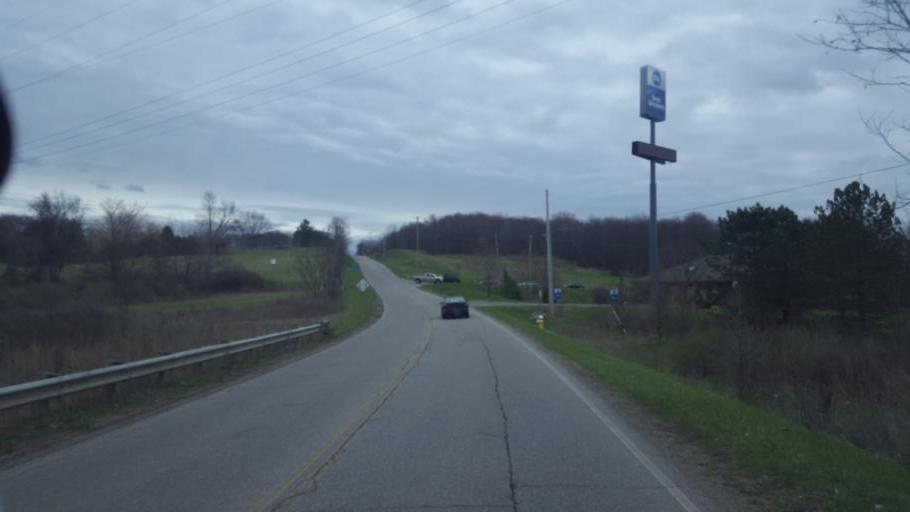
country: US
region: Ohio
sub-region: Richland County
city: Mansfield
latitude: 40.6960
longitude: -82.5084
